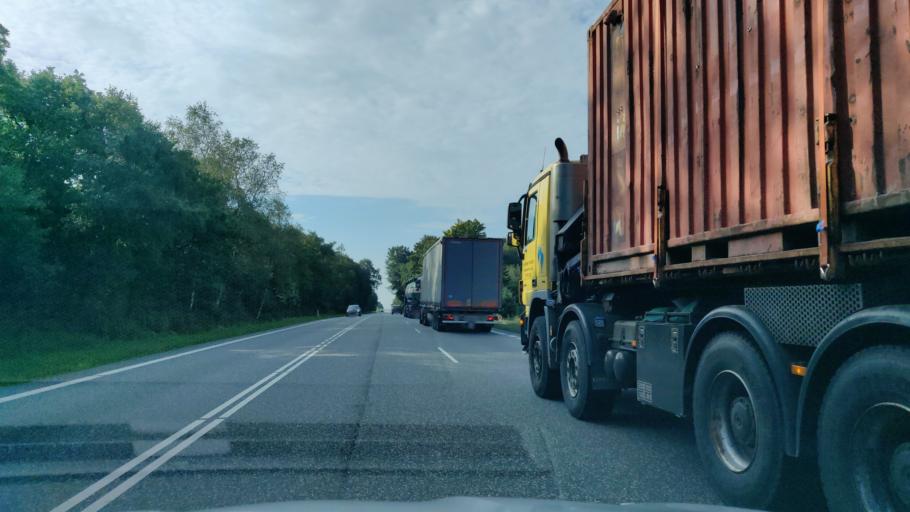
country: DK
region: North Denmark
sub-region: Vesthimmerland Kommune
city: Alestrup
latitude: 56.7297
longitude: 9.5332
